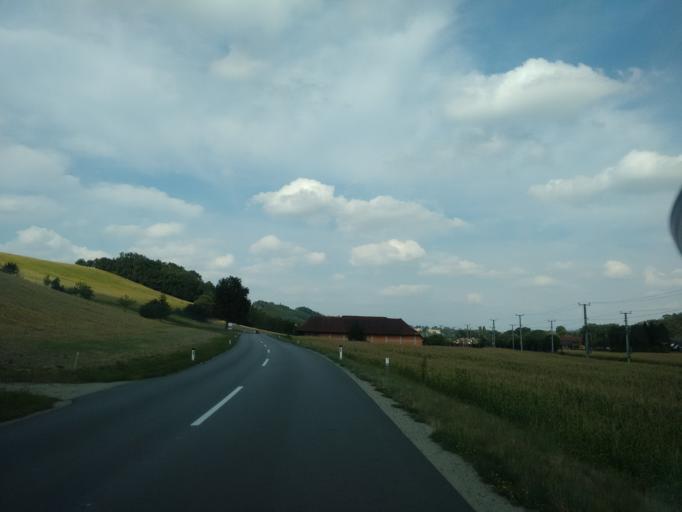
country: AT
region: Upper Austria
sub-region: Politischer Bezirk Grieskirchen
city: Bad Schallerbach
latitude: 48.2232
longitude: 13.8951
